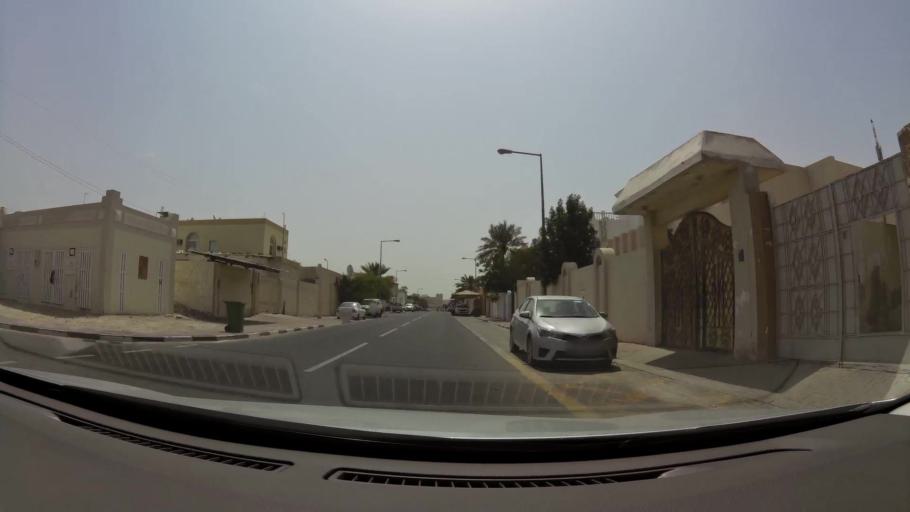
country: QA
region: Baladiyat ad Dawhah
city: Doha
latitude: 25.3173
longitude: 51.4789
